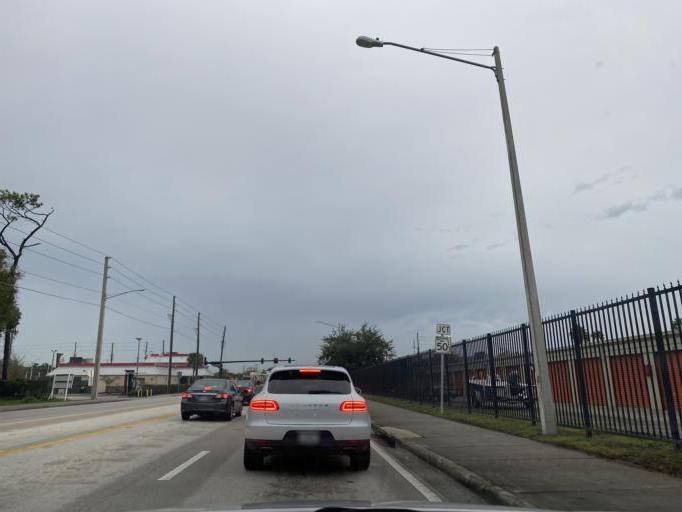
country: US
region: Florida
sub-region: Orange County
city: Winter Garden
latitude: 28.5497
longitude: -81.5836
